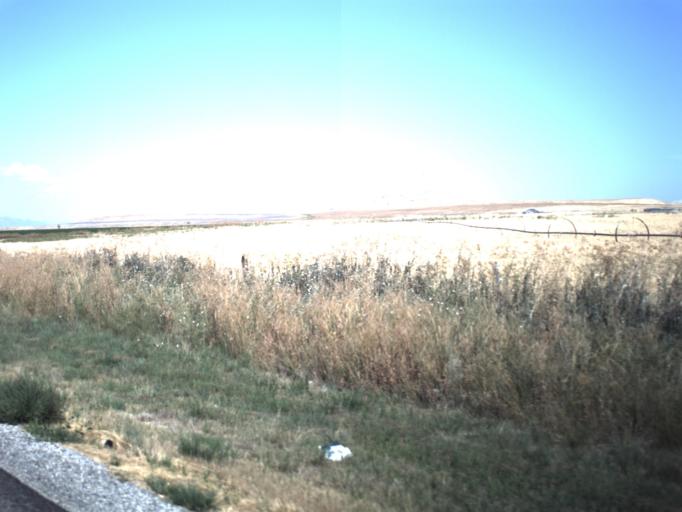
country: US
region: Utah
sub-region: Cache County
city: Benson
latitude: 41.8538
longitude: -111.9726
